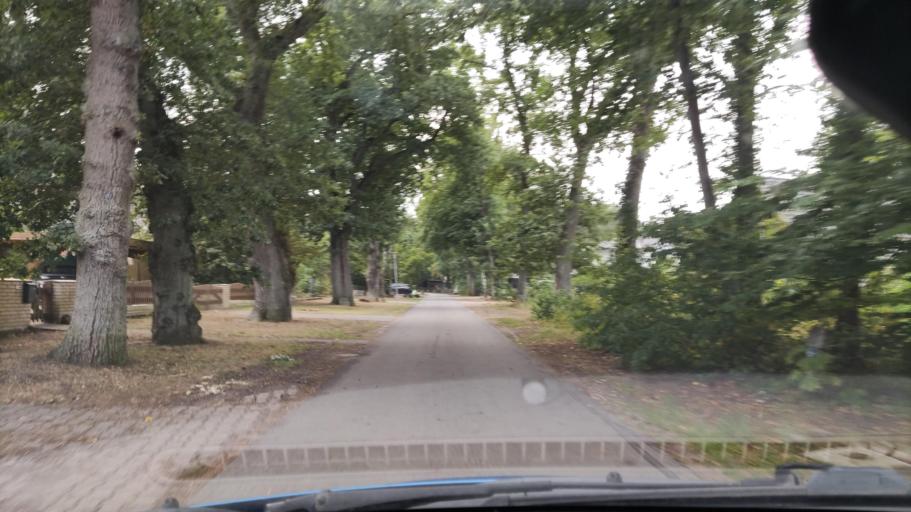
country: DE
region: Lower Saxony
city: Barum
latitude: 53.3466
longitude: 10.4102
